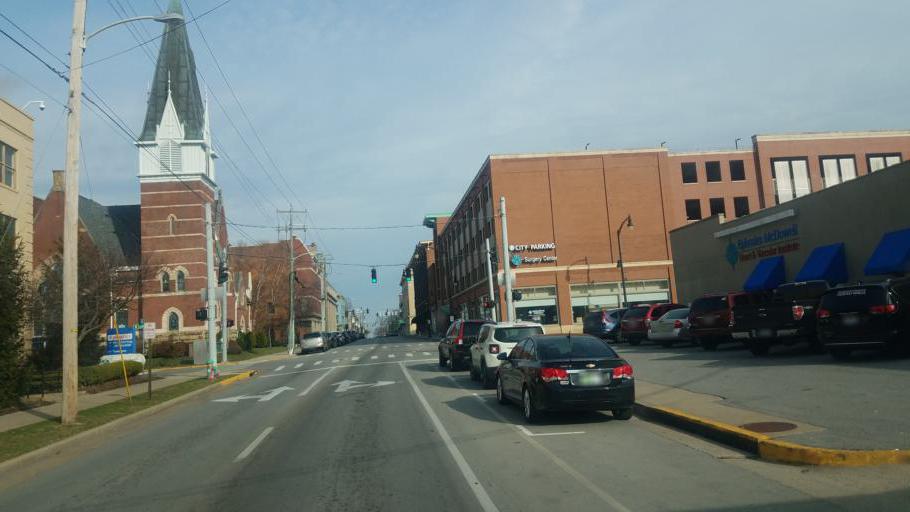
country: US
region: Kentucky
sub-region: Boyle County
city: Danville
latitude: 37.6443
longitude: -84.7727
